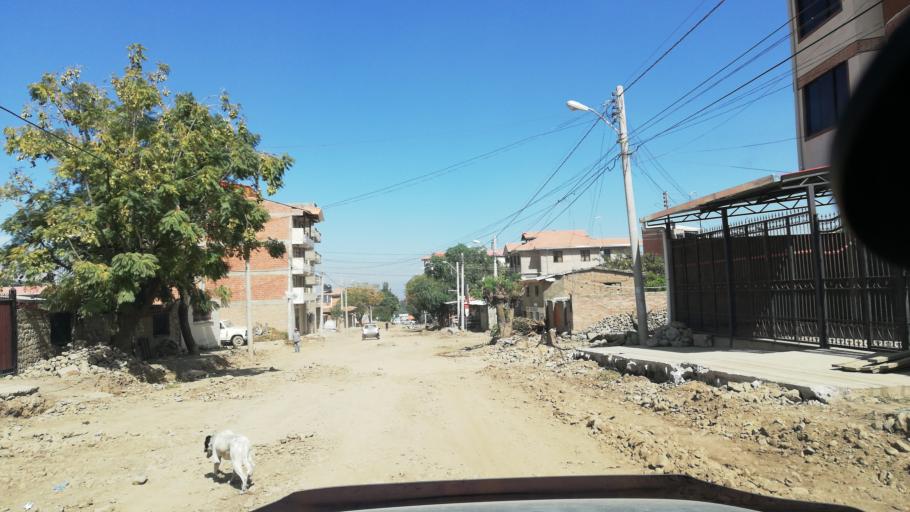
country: BO
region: Cochabamba
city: Cochabamba
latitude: -17.3339
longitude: -66.2198
